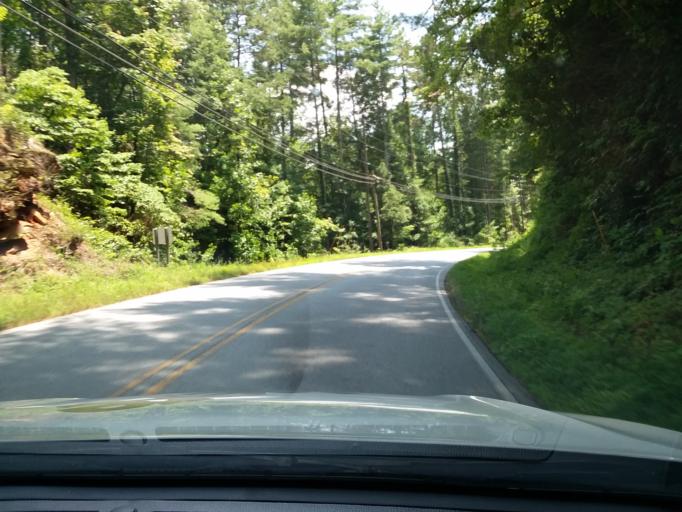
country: US
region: Georgia
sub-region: Rabun County
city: Clayton
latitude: 34.7810
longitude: -83.4162
